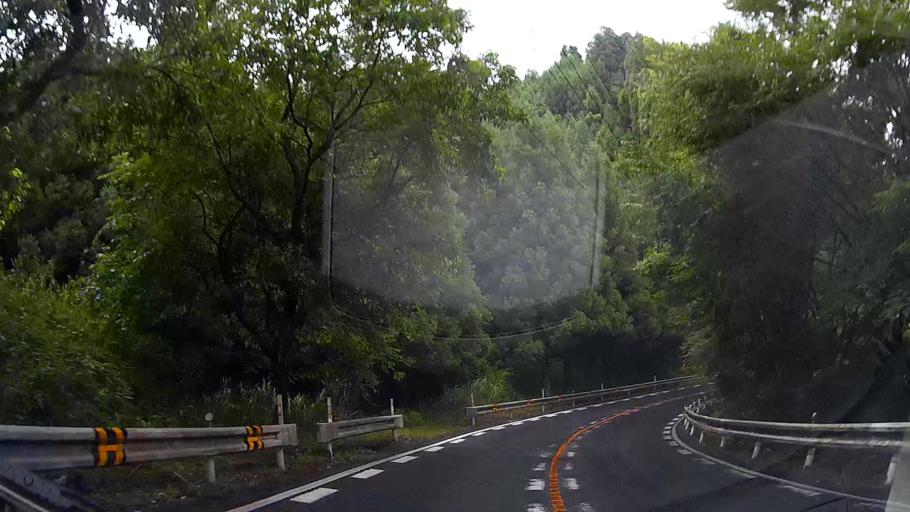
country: JP
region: Oita
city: Hita
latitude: 33.1874
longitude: 130.9973
